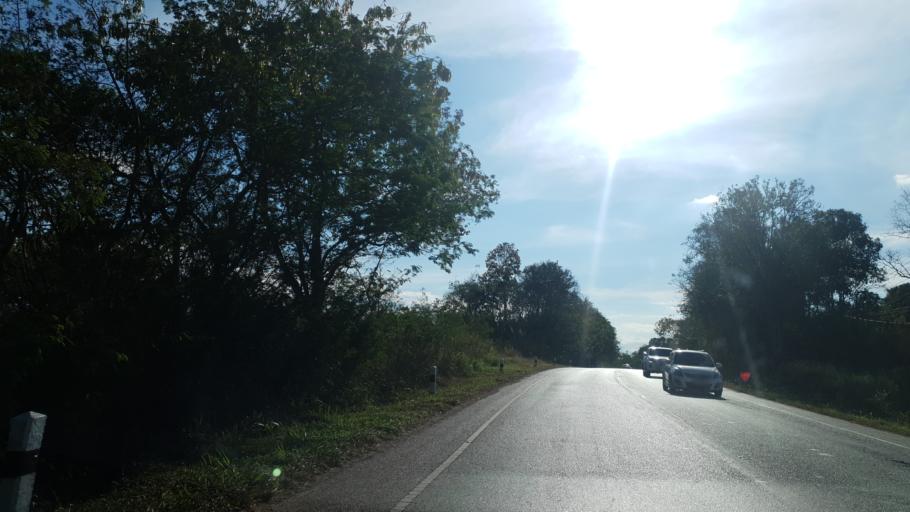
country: TH
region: Loei
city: Phu Ruea
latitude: 17.4483
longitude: 101.4785
